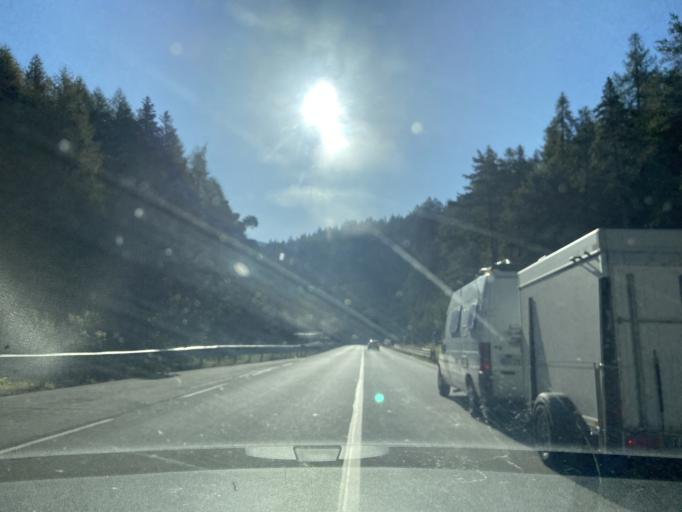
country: IT
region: Piedmont
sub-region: Provincia di Torino
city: Cesana Torinese
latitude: 44.9471
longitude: 6.7749
